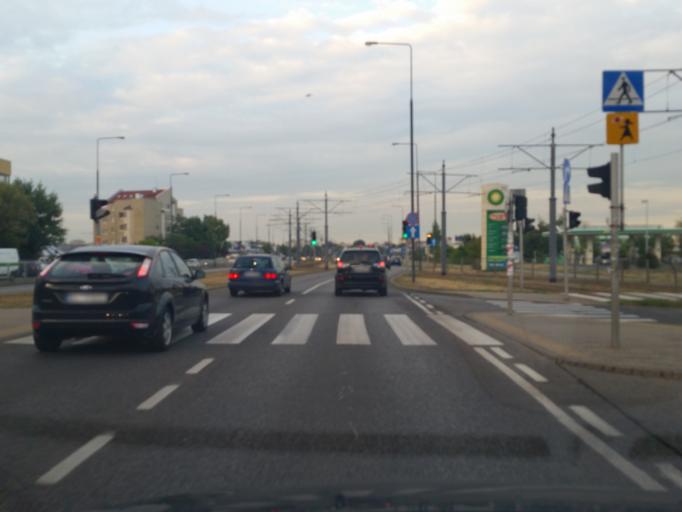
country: PL
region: Masovian Voivodeship
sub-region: Warszawa
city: Bemowo
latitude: 52.2612
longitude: 20.9247
